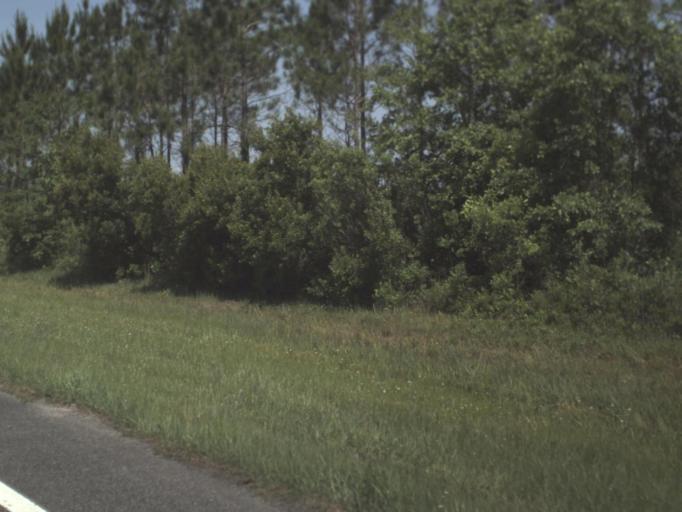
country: US
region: Florida
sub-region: Clay County
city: Middleburg
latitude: 29.9786
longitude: -81.9010
